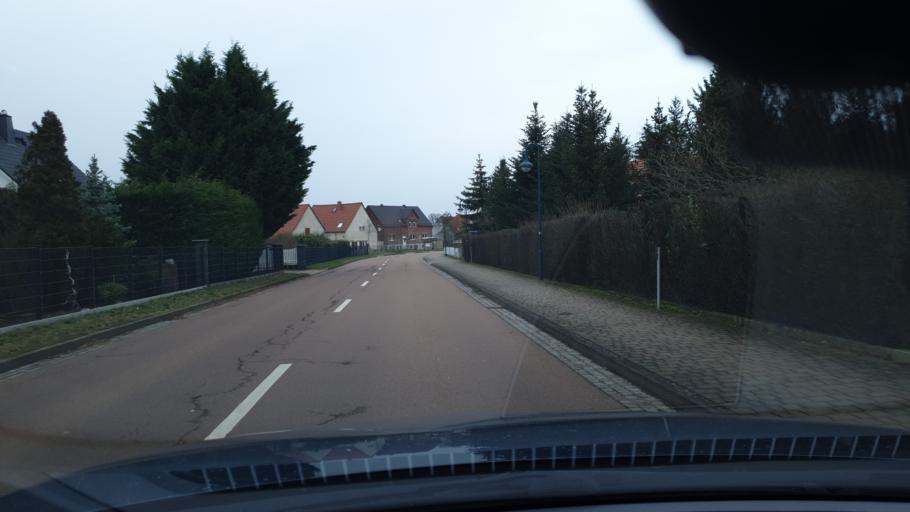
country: DE
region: Saxony-Anhalt
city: Radis
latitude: 51.7817
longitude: 12.4864
